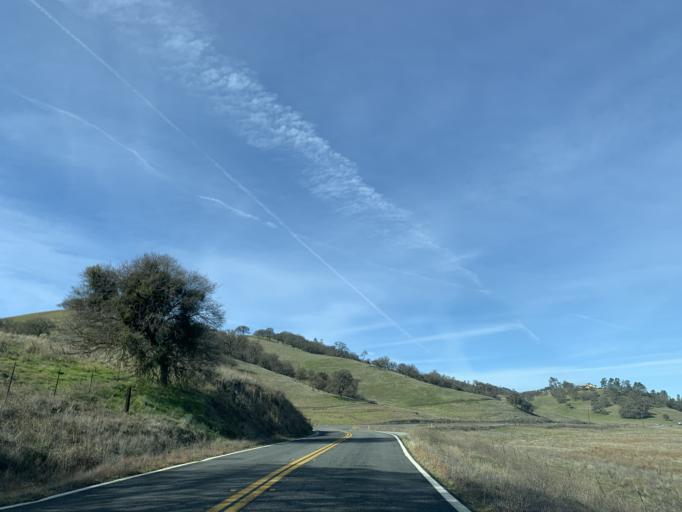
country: US
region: California
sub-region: Monterey County
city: Soledad
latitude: 36.5534
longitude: -121.1675
